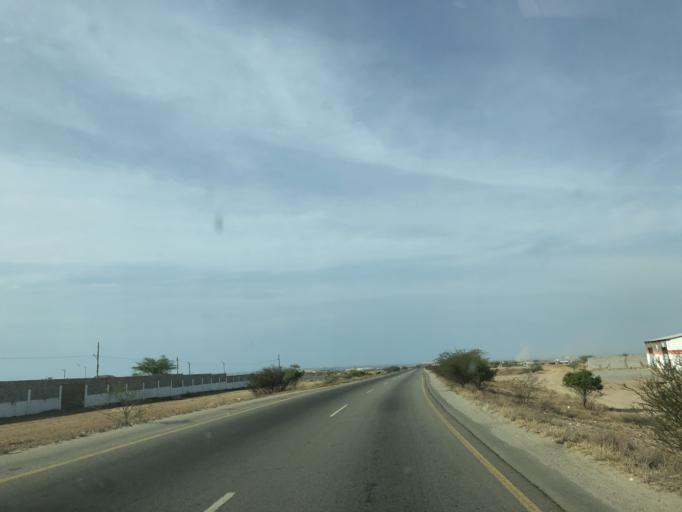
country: AO
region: Benguela
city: Benguela
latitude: -12.6850
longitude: 13.3412
